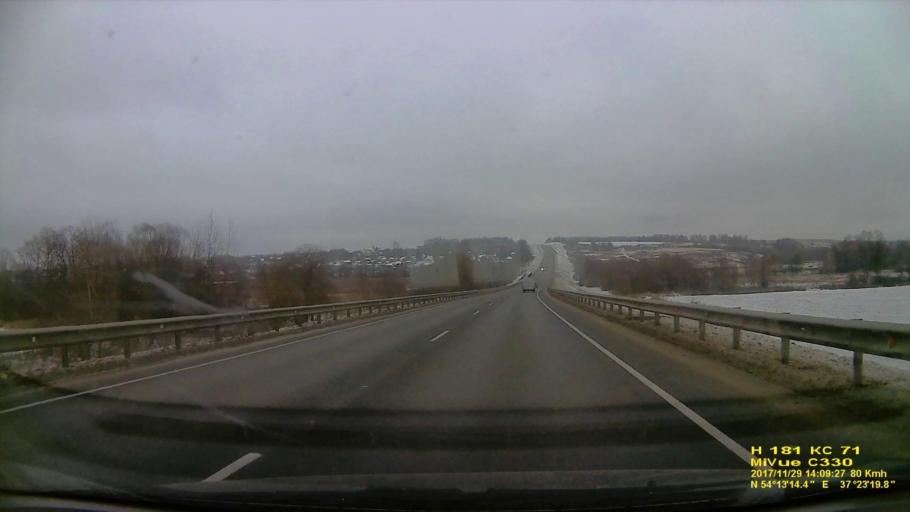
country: RU
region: Tula
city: Leninskiy
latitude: 54.2206
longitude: 37.3890
